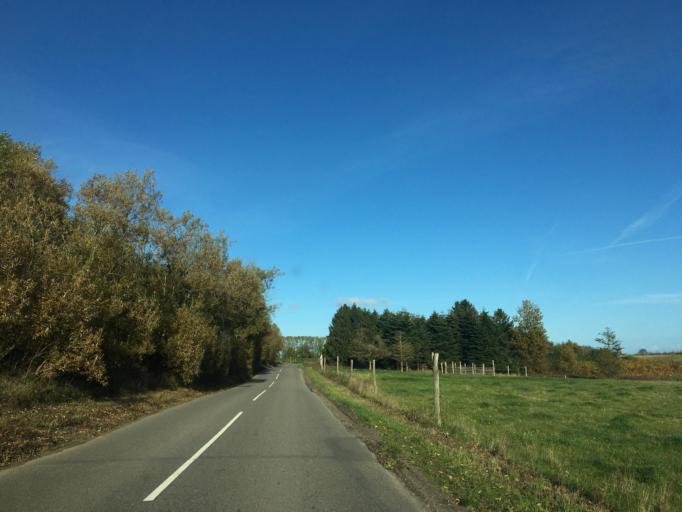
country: DK
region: Zealand
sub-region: Odsherred Kommune
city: Asnaes
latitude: 55.8400
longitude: 11.5582
